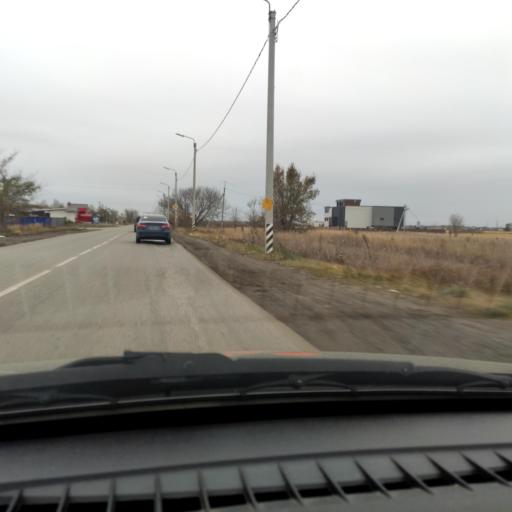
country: RU
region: Samara
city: Podstepki
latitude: 53.5220
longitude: 49.1814
